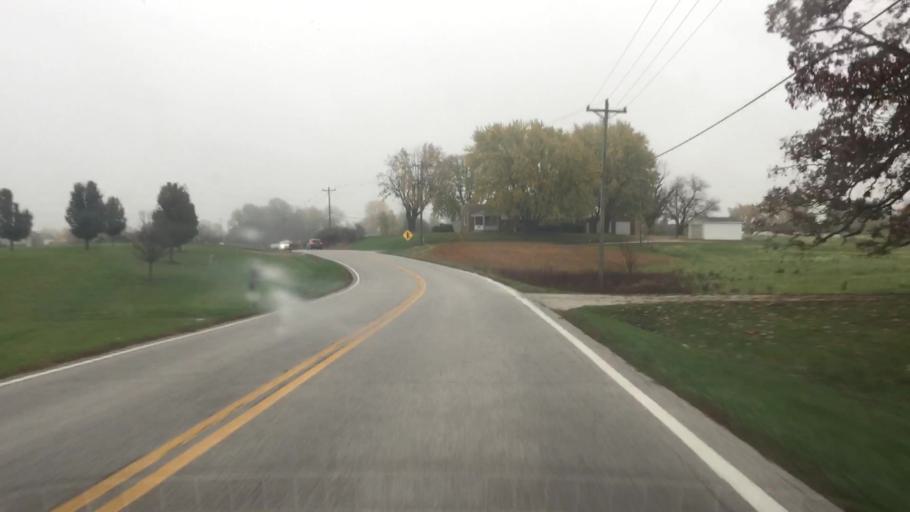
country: US
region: Missouri
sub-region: Callaway County
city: Fulton
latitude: 38.8583
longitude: -91.9960
